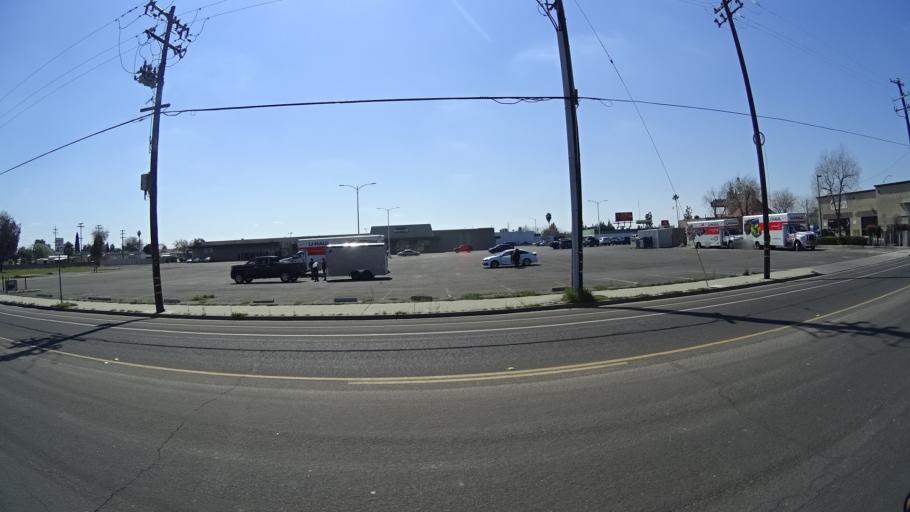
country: US
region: California
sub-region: Fresno County
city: Fresno
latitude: 36.8014
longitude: -119.7895
